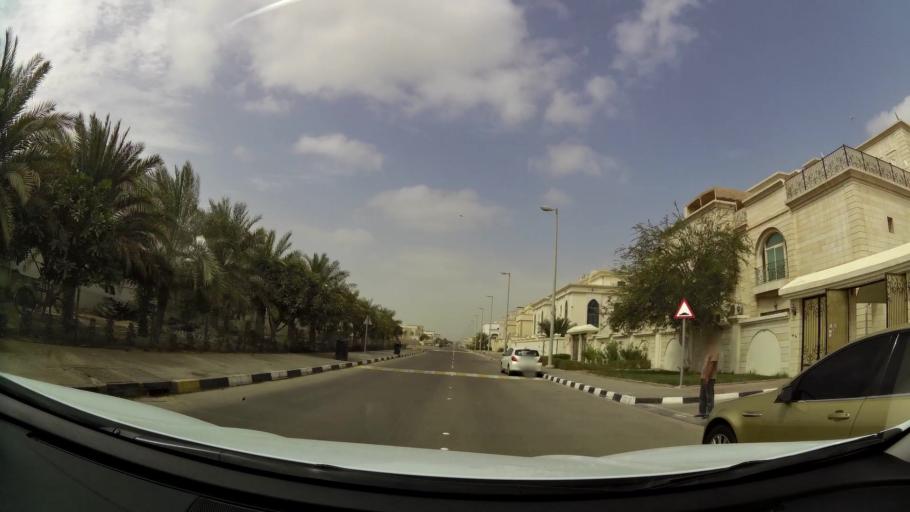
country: AE
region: Abu Dhabi
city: Abu Dhabi
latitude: 24.3947
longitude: 54.4990
